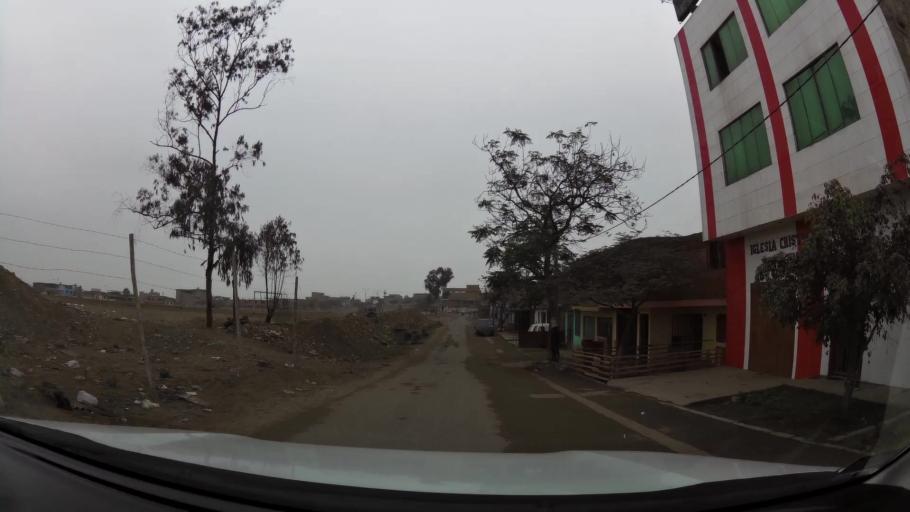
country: PE
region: Lima
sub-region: Lima
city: Surco
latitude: -12.1831
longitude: -76.9254
